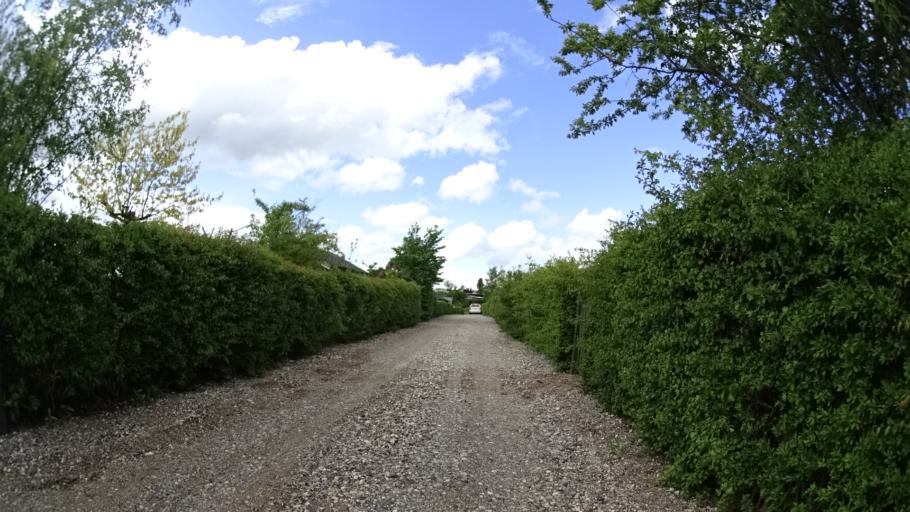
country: DK
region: Central Jutland
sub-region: Arhus Kommune
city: Stavtrup
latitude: 56.1375
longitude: 10.1431
